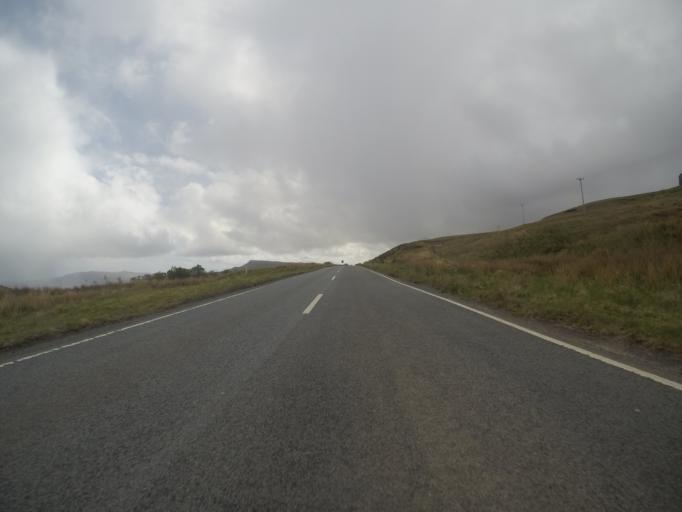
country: GB
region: Scotland
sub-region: Highland
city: Portree
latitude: 57.5047
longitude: -6.1525
